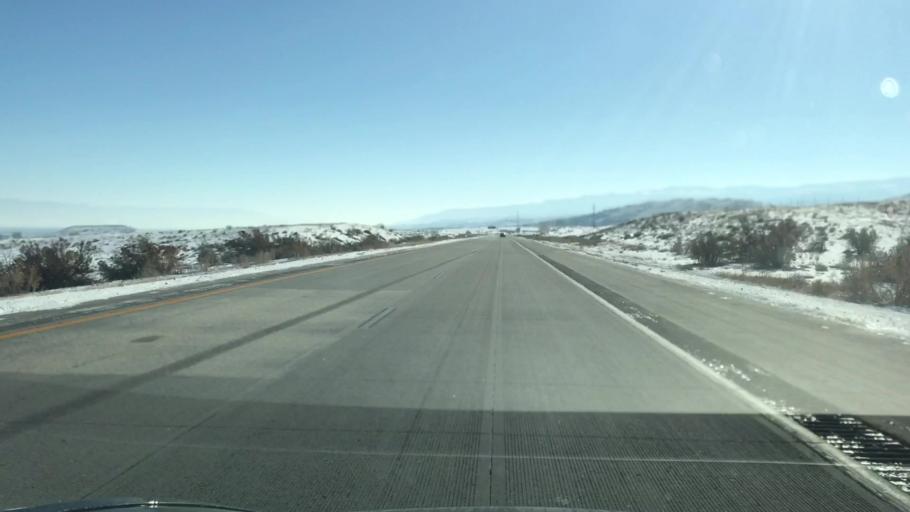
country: US
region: Colorado
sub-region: Mesa County
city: Loma
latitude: 39.1864
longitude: -108.8344
